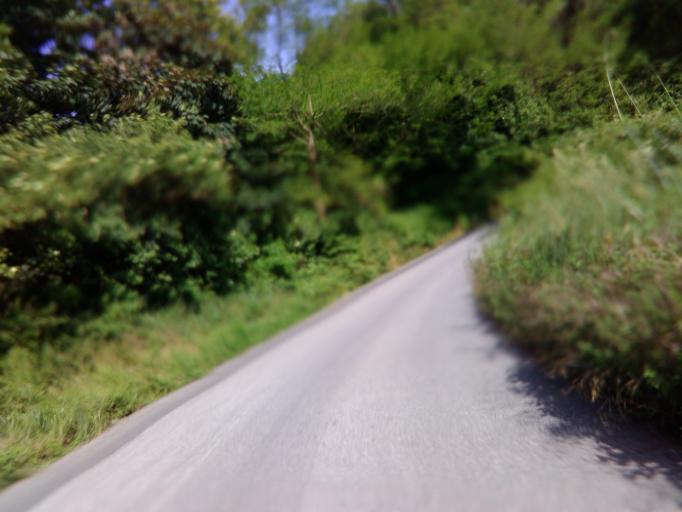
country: IT
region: Tuscany
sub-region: Provincia di Massa-Carrara
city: Fosdinovo
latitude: 44.1357
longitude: 10.0315
